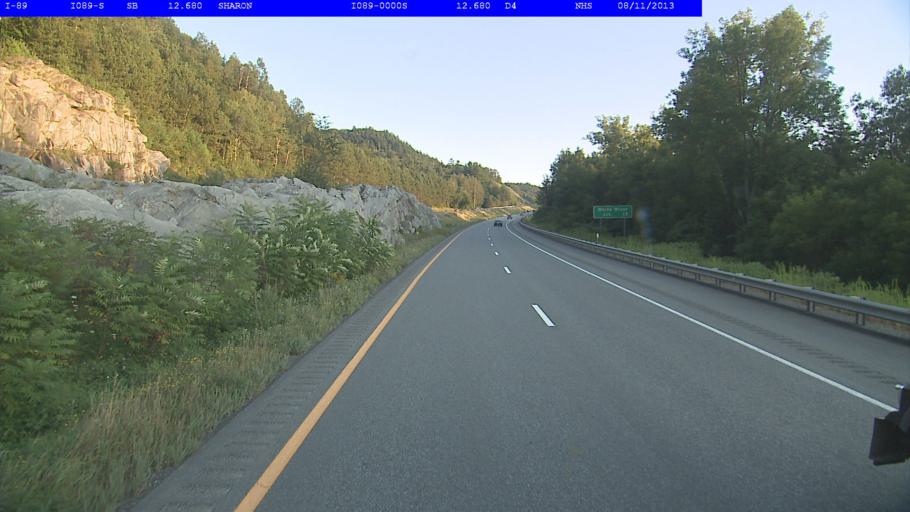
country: US
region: Vermont
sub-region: Windsor County
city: Woodstock
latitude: 43.7779
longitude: -72.4448
